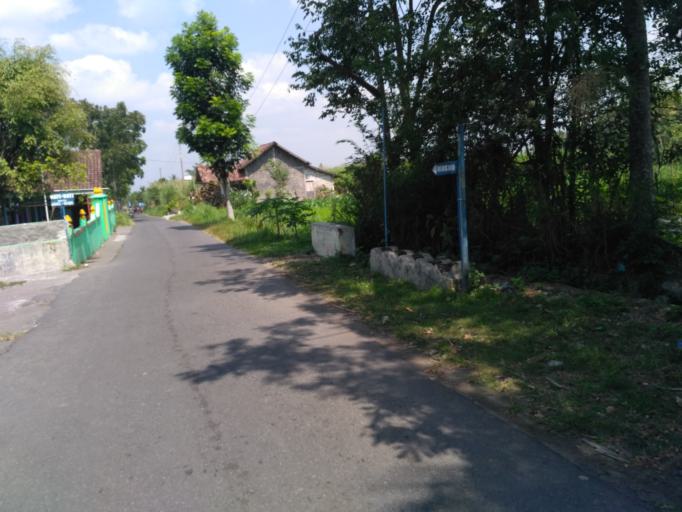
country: ID
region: Daerah Istimewa Yogyakarta
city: Depok
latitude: -7.7113
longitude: 110.4240
